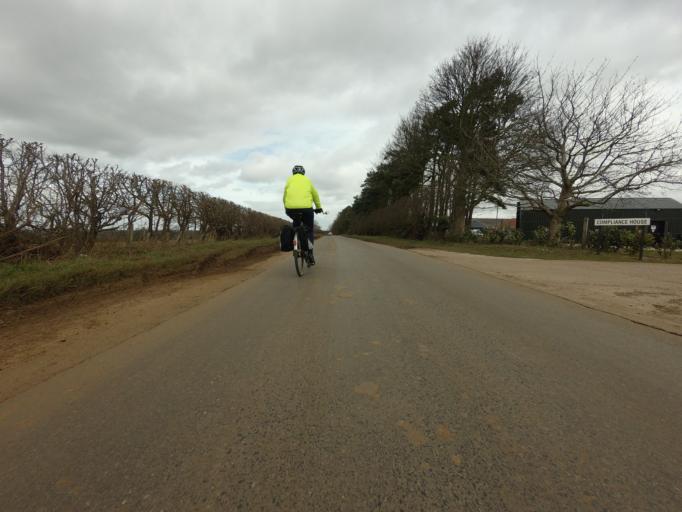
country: GB
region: England
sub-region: Lincolnshire
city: Grantham
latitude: 52.8828
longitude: -0.6631
